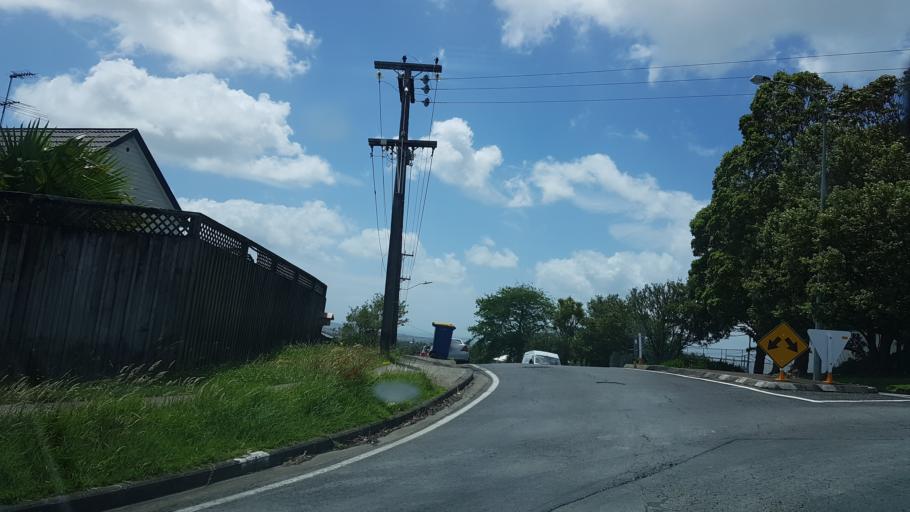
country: NZ
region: Auckland
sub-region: Auckland
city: North Shore
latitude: -36.8062
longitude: 174.7065
